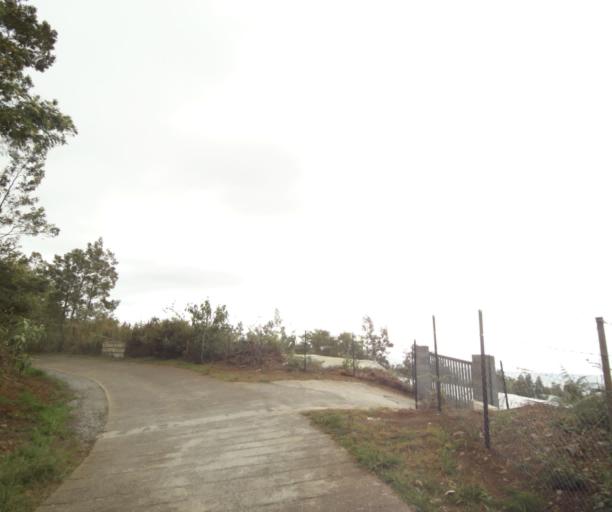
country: RE
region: Reunion
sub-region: Reunion
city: Saint-Paul
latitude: -21.0114
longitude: 55.3540
